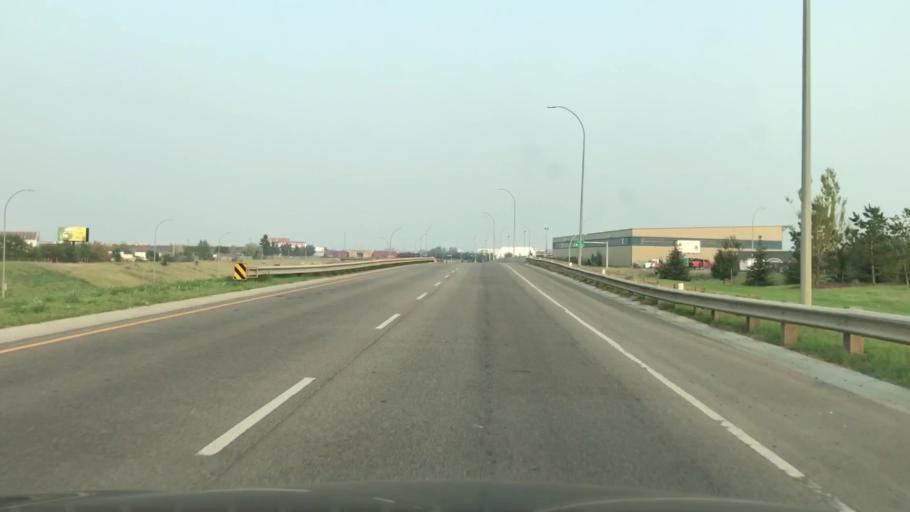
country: CA
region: Alberta
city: Edmonton
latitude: 53.5166
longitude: -113.4335
